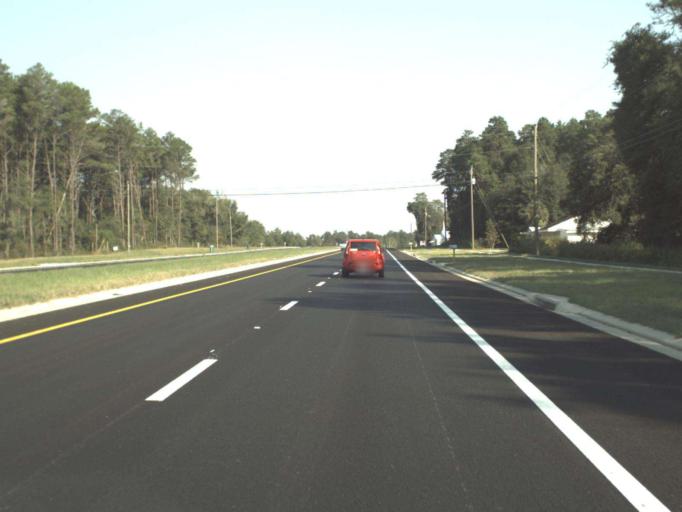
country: US
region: Florida
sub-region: Holmes County
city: Bonifay
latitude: 30.5728
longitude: -85.8073
